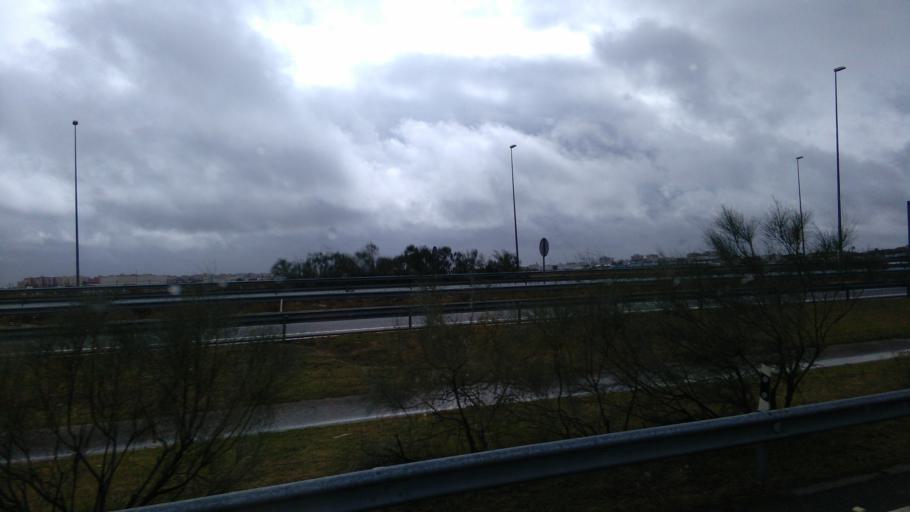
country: ES
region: Madrid
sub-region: Provincia de Madrid
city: Alcorcon
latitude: 40.3128
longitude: -3.8255
